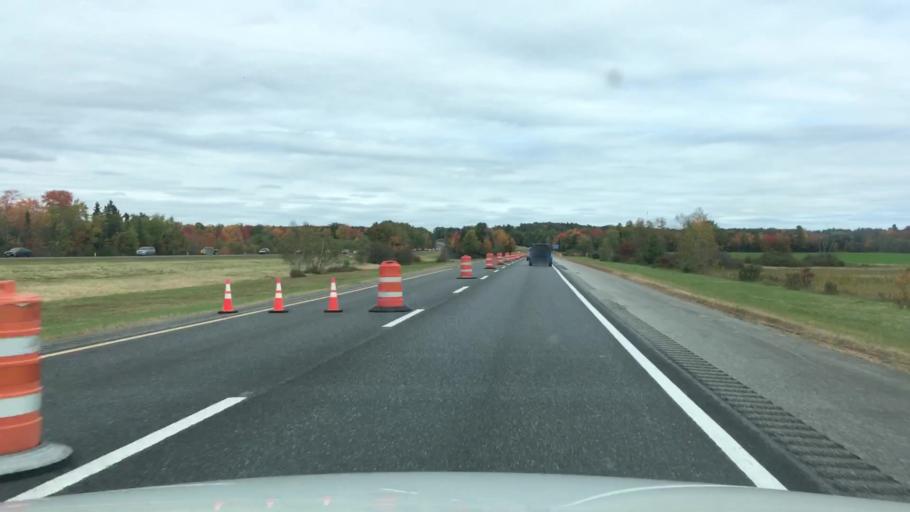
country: US
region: Maine
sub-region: Sagadahoc County
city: Richmond
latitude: 44.1510
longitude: -69.8383
